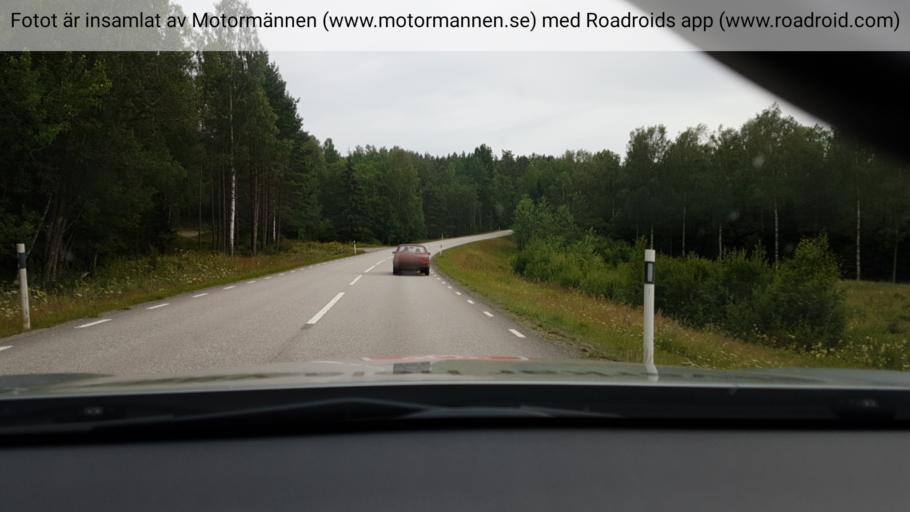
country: SE
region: Vaestra Goetaland
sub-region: Bengtsfors Kommun
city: Dals Langed
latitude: 58.9022
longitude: 12.2185
